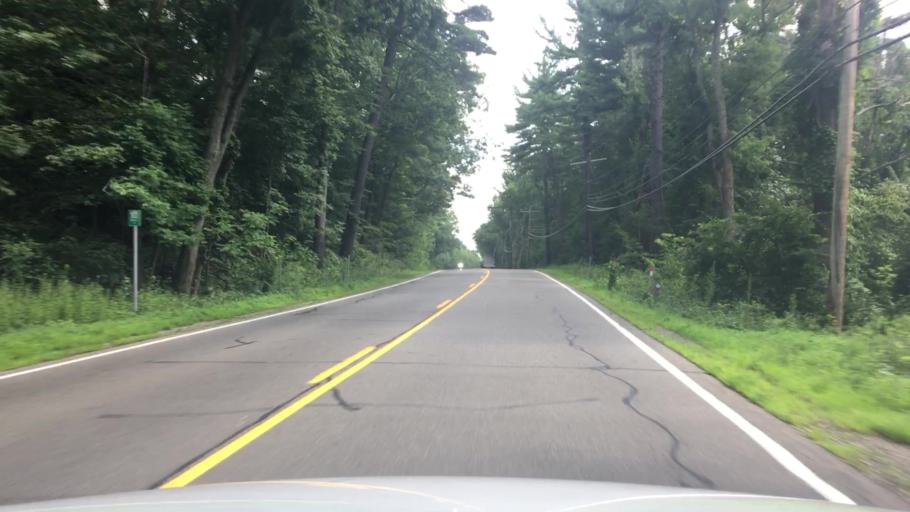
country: US
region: New Hampshire
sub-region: Rockingham County
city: Auburn
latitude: 42.9688
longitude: -71.3644
